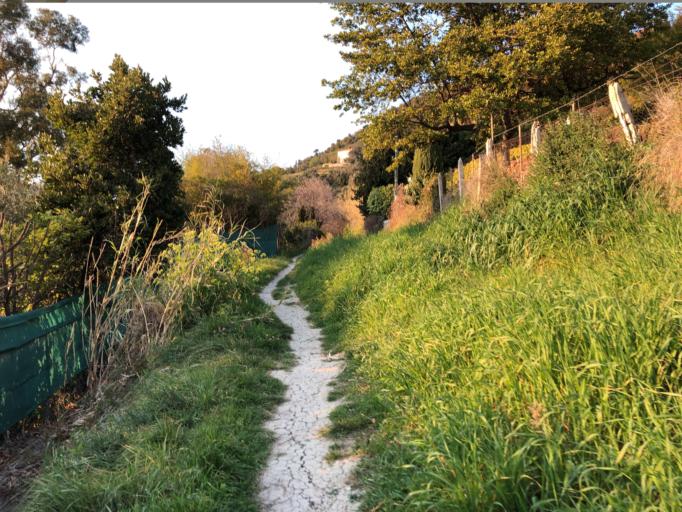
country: FR
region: Provence-Alpes-Cote d'Azur
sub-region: Departement des Alpes-Maritimes
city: Villefranche-sur-Mer
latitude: 43.7193
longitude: 7.2994
